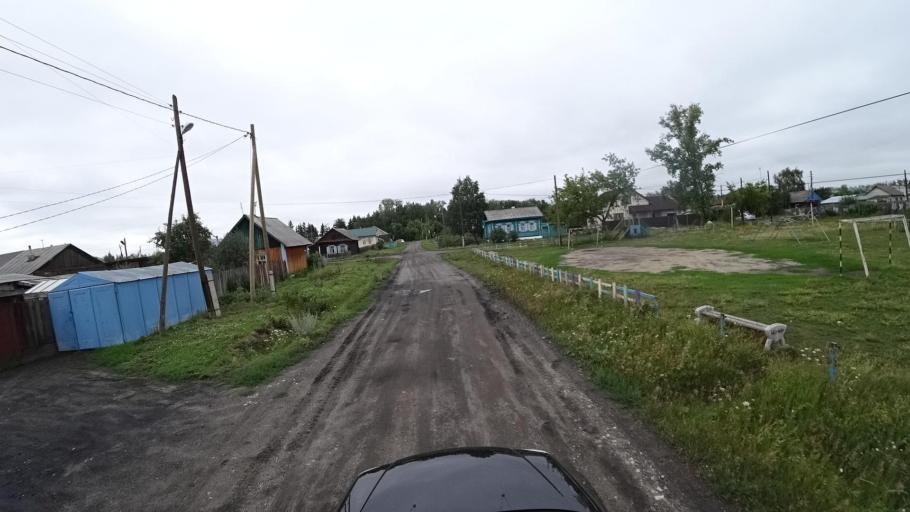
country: RU
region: Sverdlovsk
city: Kamyshlov
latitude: 56.8476
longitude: 62.7634
